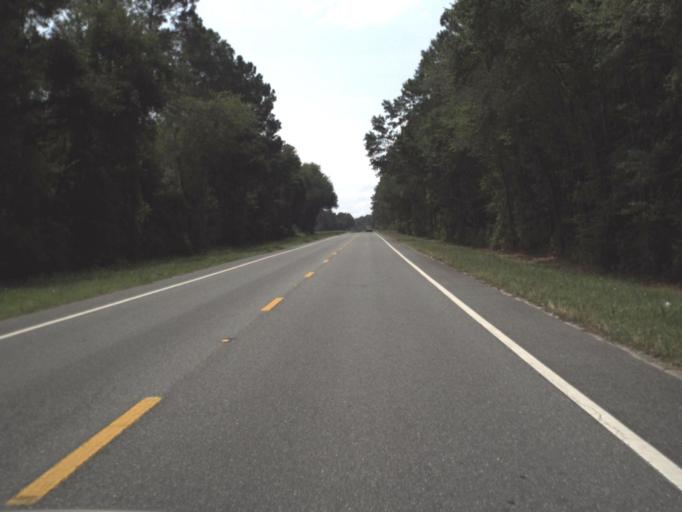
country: US
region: Florida
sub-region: Hamilton County
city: Jasper
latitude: 30.5622
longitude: -83.0710
